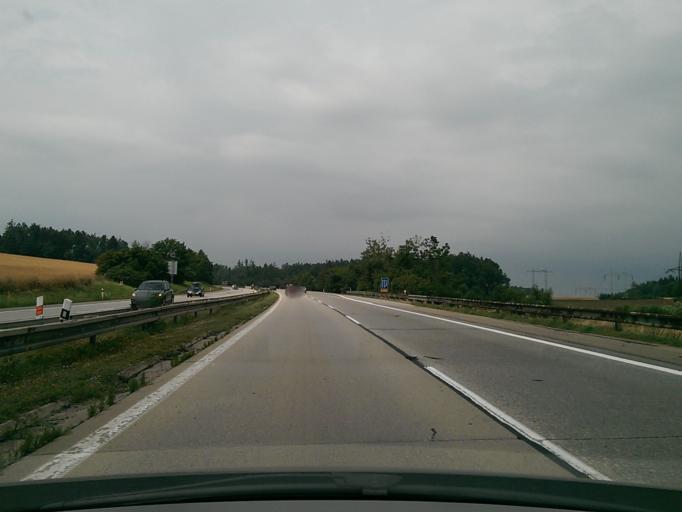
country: CZ
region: South Moravian
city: Zbraslav
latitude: 49.2560
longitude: 16.3433
